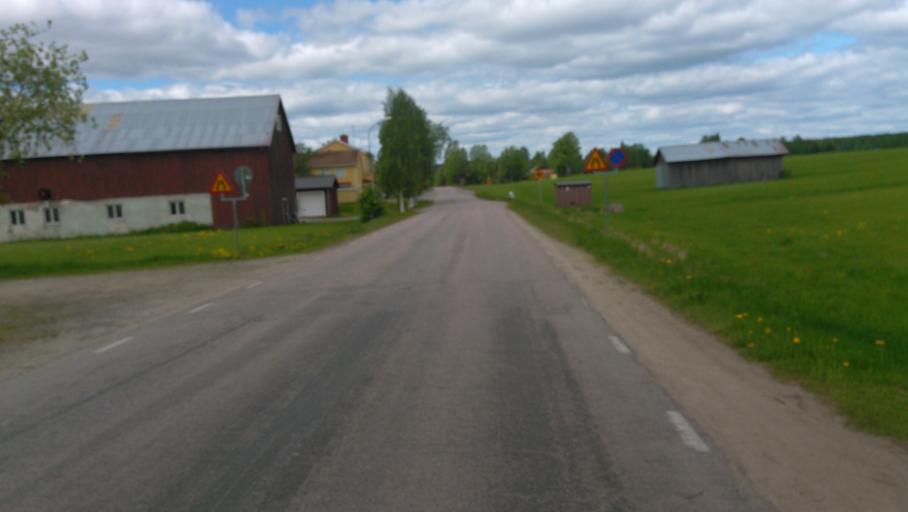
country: SE
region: Vaesterbotten
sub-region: Umea Kommun
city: Roback
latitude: 63.8672
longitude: 20.0744
